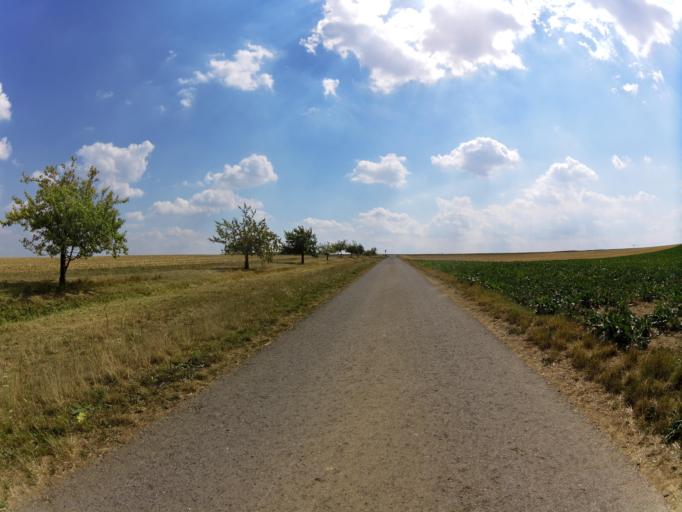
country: DE
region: Bavaria
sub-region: Regierungsbezirk Unterfranken
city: Ochsenfurt
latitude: 49.6389
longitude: 10.0560
